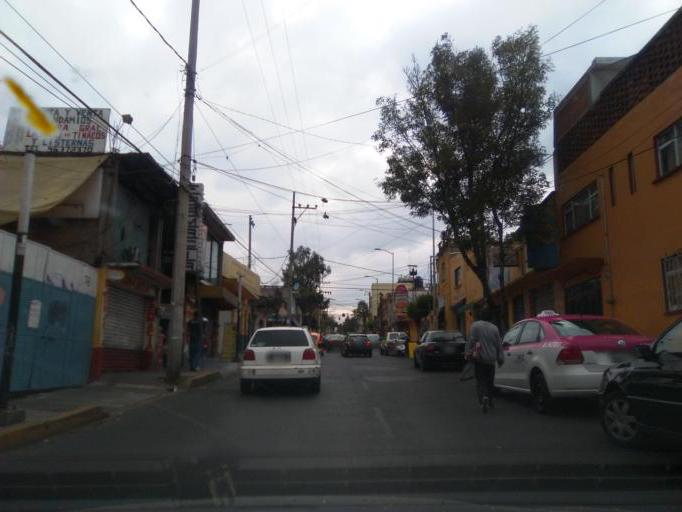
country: MX
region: Mexico City
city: Alvaro Obregon
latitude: 19.3718
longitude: -99.2176
